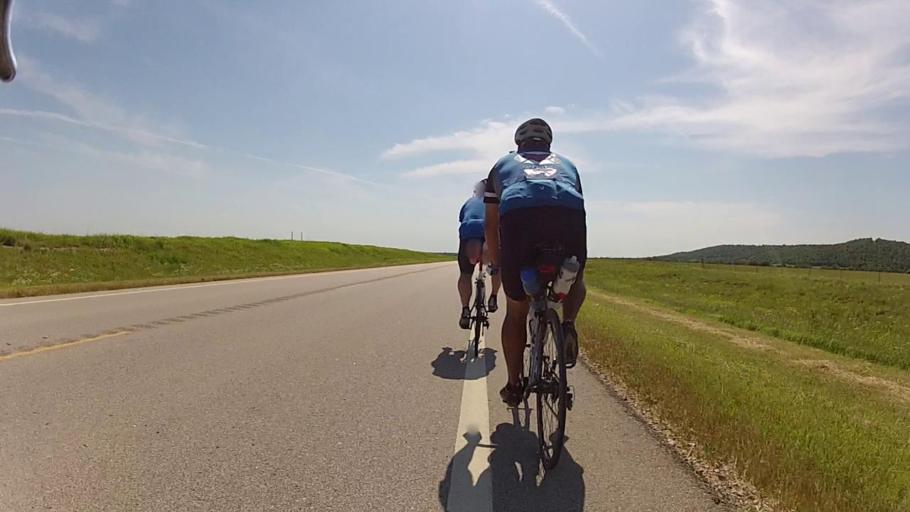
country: US
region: Kansas
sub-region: Chautauqua County
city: Sedan
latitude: 37.1068
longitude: -96.5567
